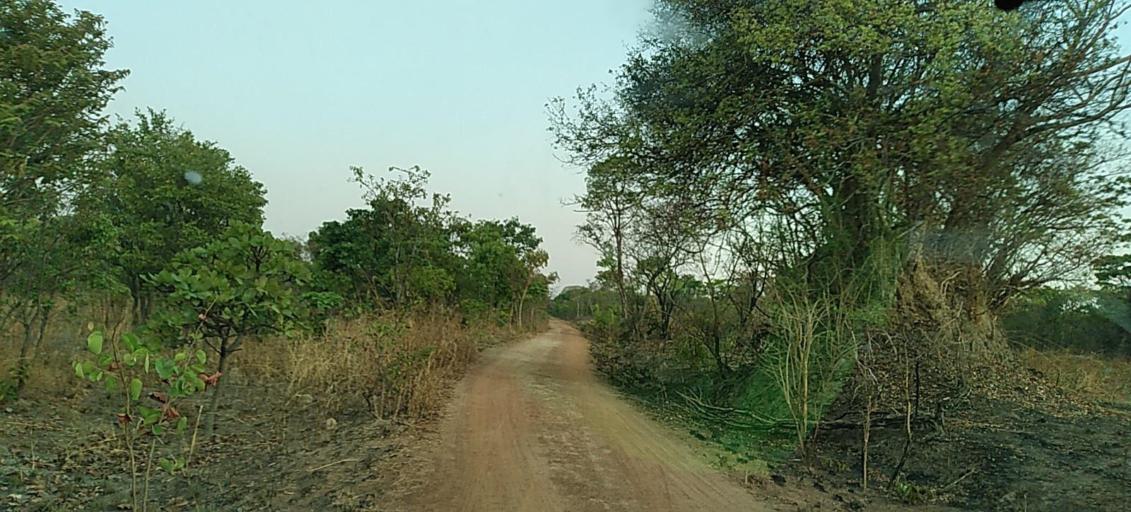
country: ZM
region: North-Western
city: Kalengwa
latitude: -13.1132
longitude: 25.1684
